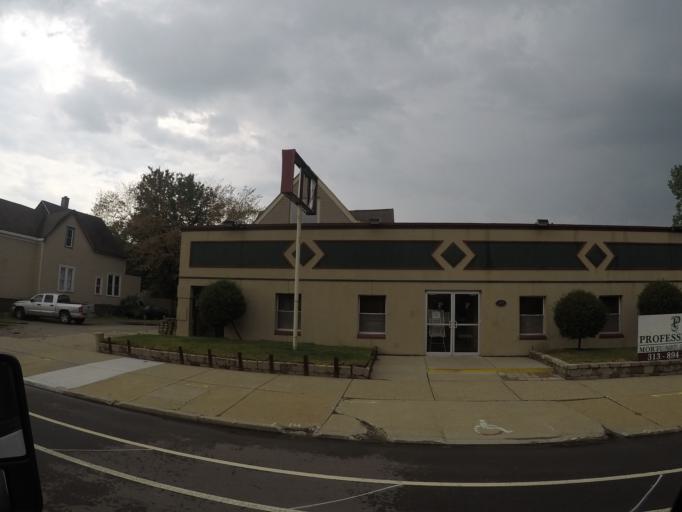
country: US
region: Michigan
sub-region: Wayne County
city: Dearborn
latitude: 42.3293
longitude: -83.1192
